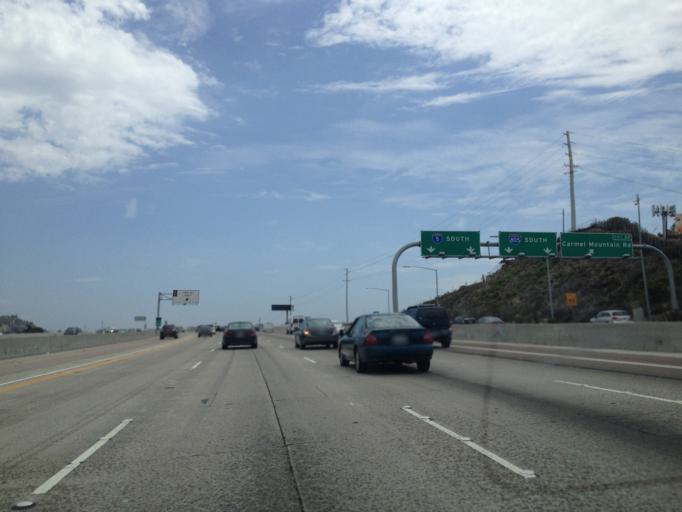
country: US
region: California
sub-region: San Diego County
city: Del Mar
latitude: 32.9220
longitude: -117.2382
